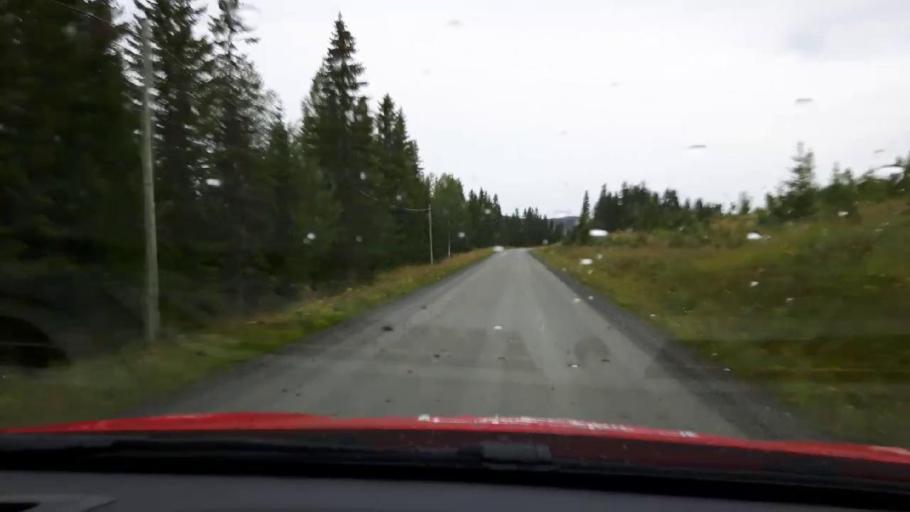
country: SE
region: Jaemtland
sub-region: Are Kommun
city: Are
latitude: 63.4259
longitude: 12.8127
